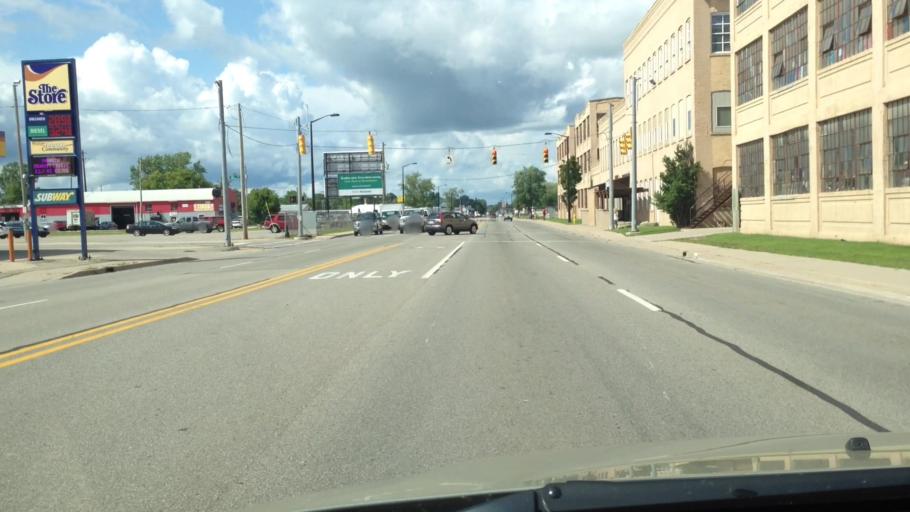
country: US
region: Michigan
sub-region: Menominee County
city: Menominee
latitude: 45.1254
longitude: -87.6130
